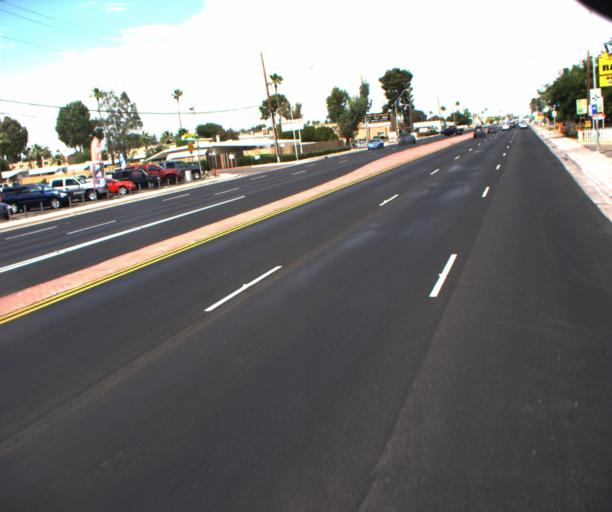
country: US
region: Arizona
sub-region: Maricopa County
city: Mesa
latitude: 33.4010
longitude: -111.8400
